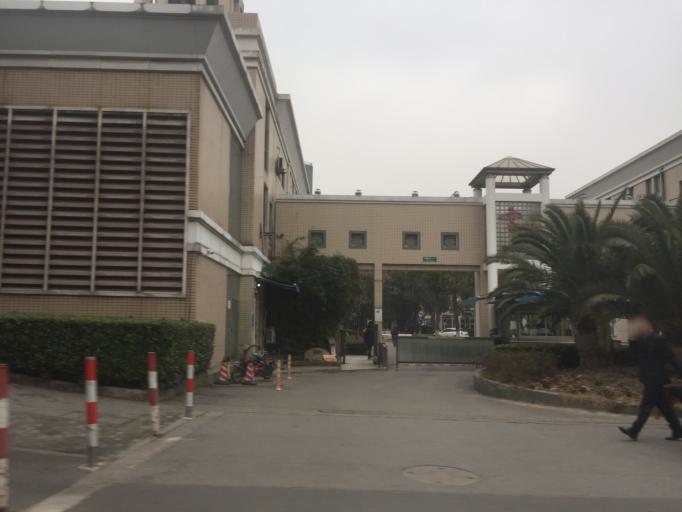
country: CN
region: Shanghai Shi
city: Luwan
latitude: 31.1851
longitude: 121.4966
